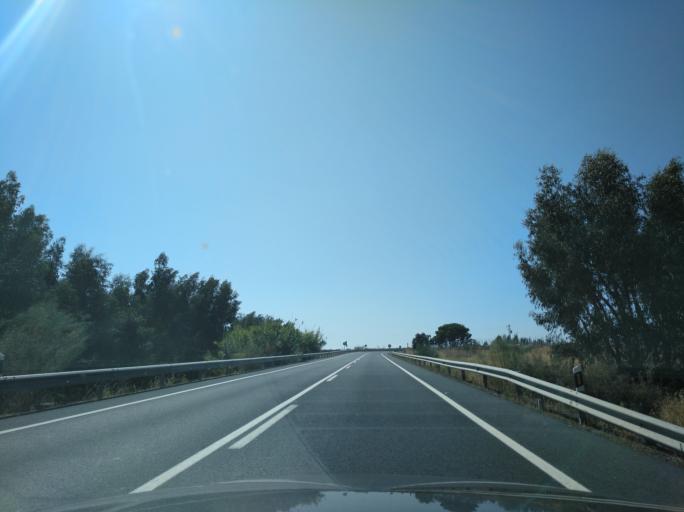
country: ES
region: Andalusia
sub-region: Provincia de Huelva
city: San Bartolome de la Torre
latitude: 37.4283
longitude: -7.0925
